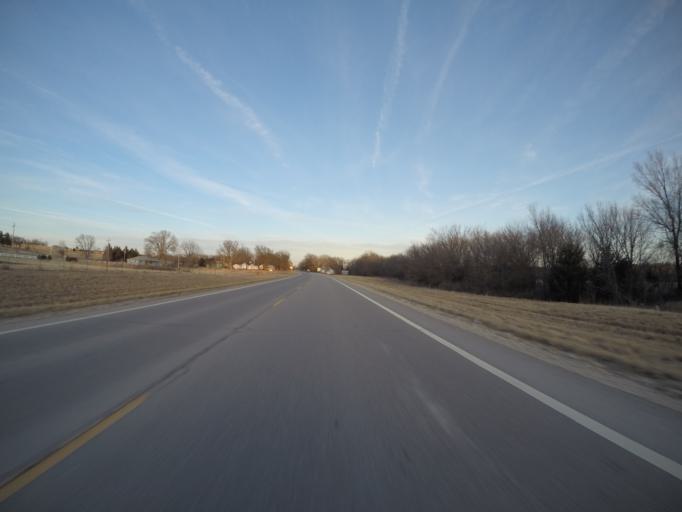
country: US
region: Kansas
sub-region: Morris County
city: Council Grove
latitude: 38.6550
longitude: -96.5120
